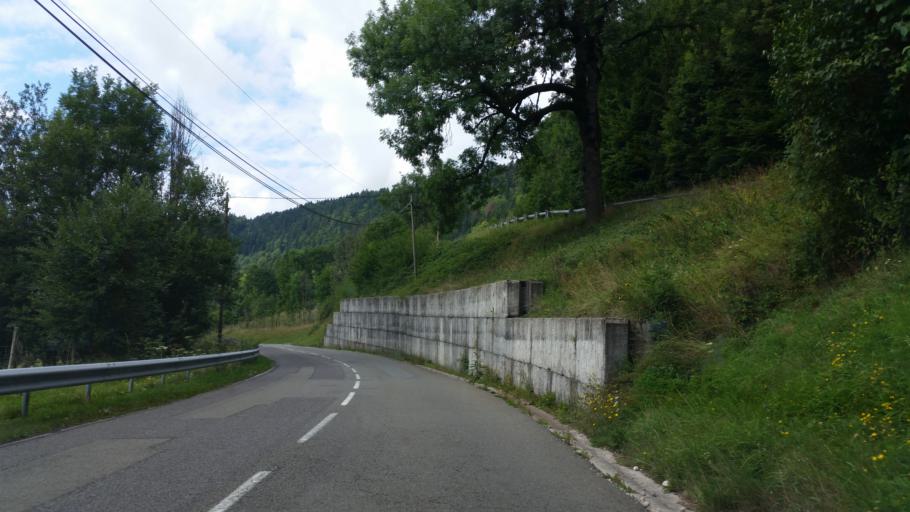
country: FR
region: Franche-Comte
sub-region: Departement du Doubs
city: Charquemont
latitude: 47.1784
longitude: 6.8387
